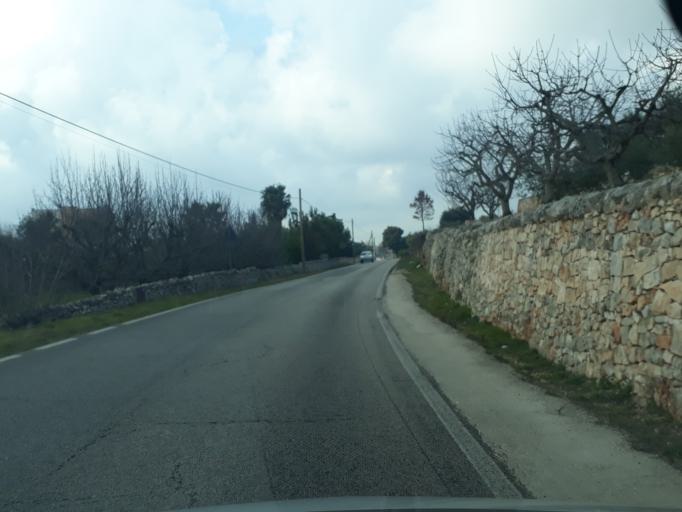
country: IT
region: Apulia
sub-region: Provincia di Bari
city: Locorotondo
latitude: 40.7536
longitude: 17.3622
